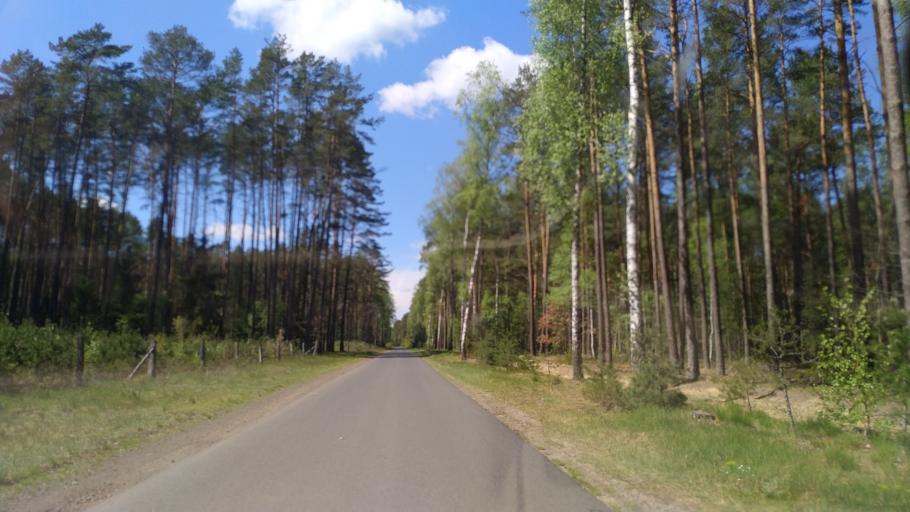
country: PL
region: Greater Poland Voivodeship
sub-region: Powiat zlotowski
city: Tarnowka
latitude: 53.2663
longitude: 16.8890
